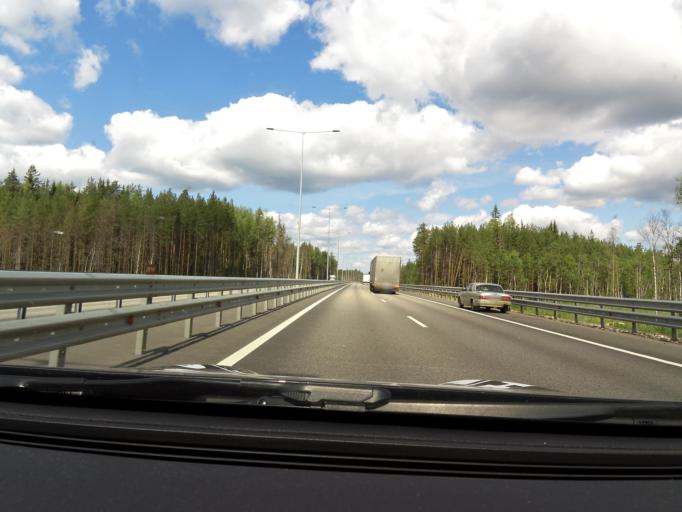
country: RU
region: Tverskaya
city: Krasnomayskiy
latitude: 57.5009
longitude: 34.2967
